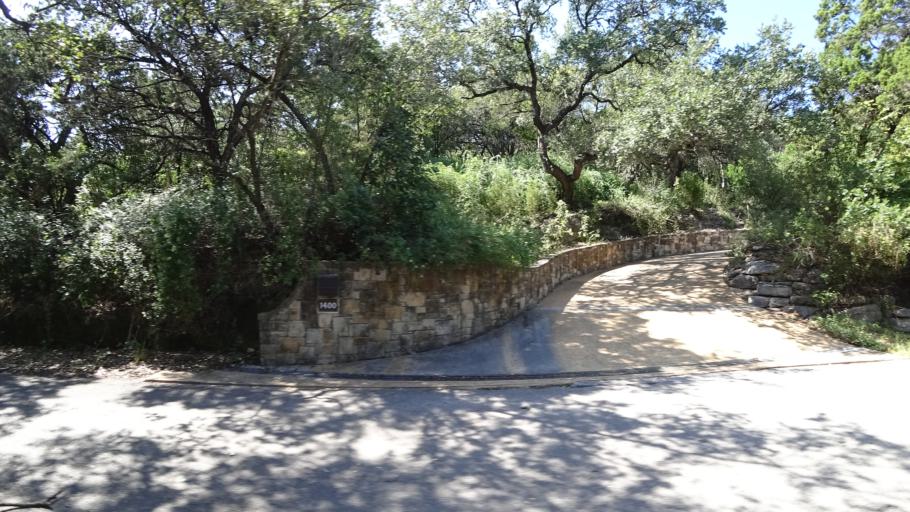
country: US
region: Texas
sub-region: Travis County
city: West Lake Hills
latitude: 30.2953
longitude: -97.7974
